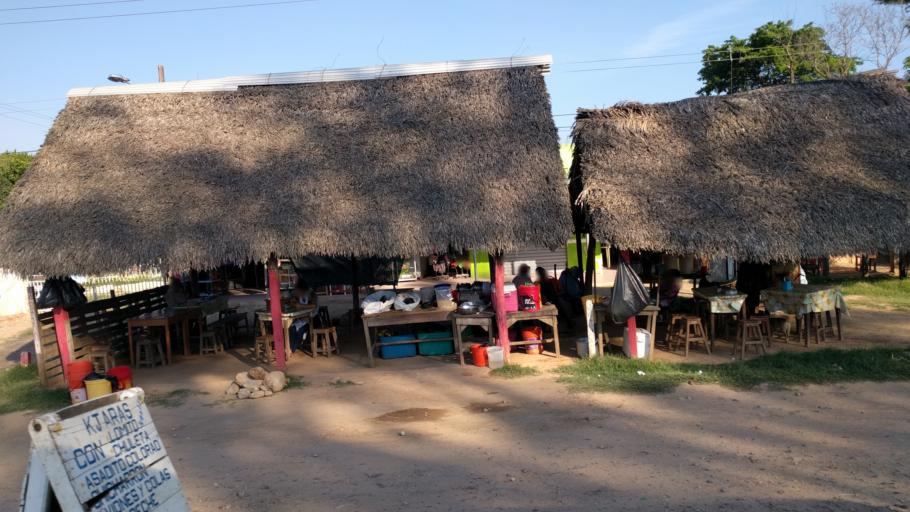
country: BO
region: Santa Cruz
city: Jorochito
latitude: -18.1423
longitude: -63.4802
